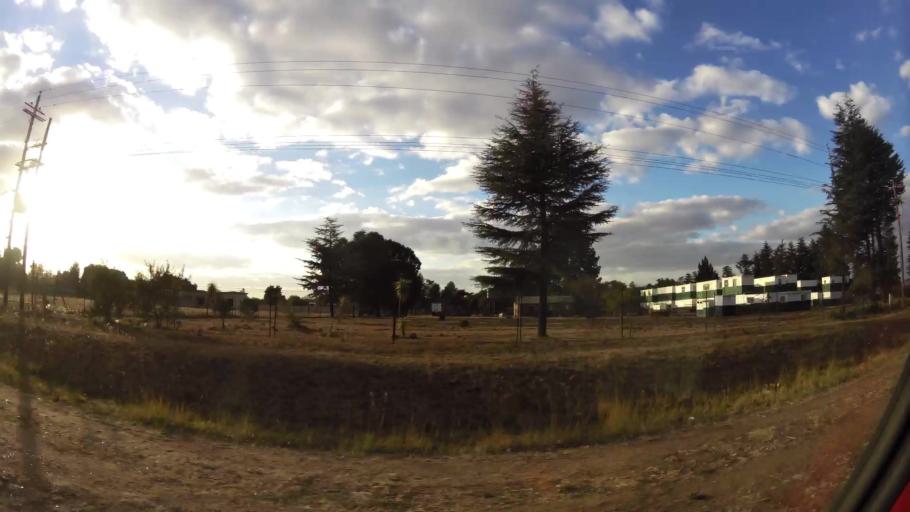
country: ZA
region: Gauteng
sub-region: City of Johannesburg Metropolitan Municipality
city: Midrand
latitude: -25.9581
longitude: 28.1588
